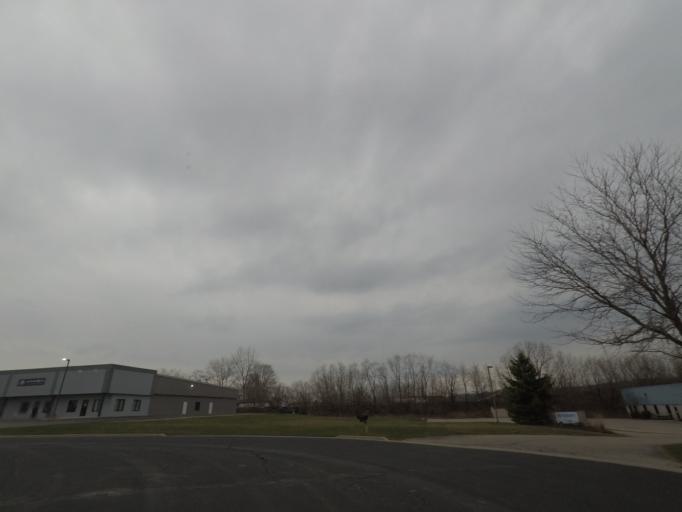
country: US
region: Wisconsin
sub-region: Dane County
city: Middleton
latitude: 43.0990
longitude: -89.5419
